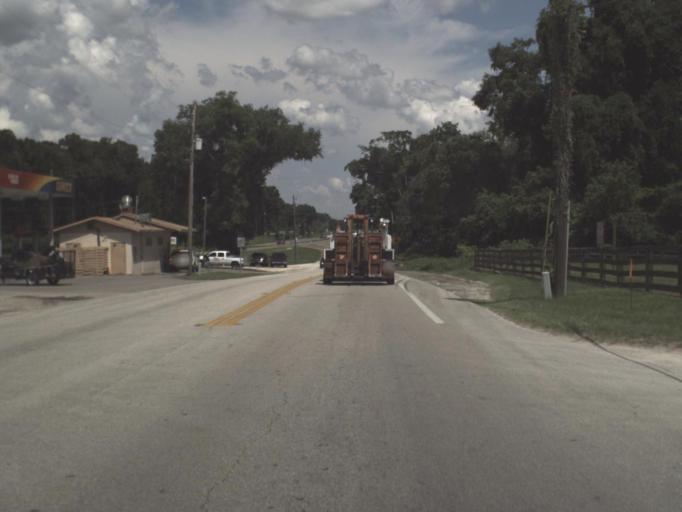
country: US
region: Florida
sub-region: Alachua County
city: High Springs
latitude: 29.8243
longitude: -82.5909
